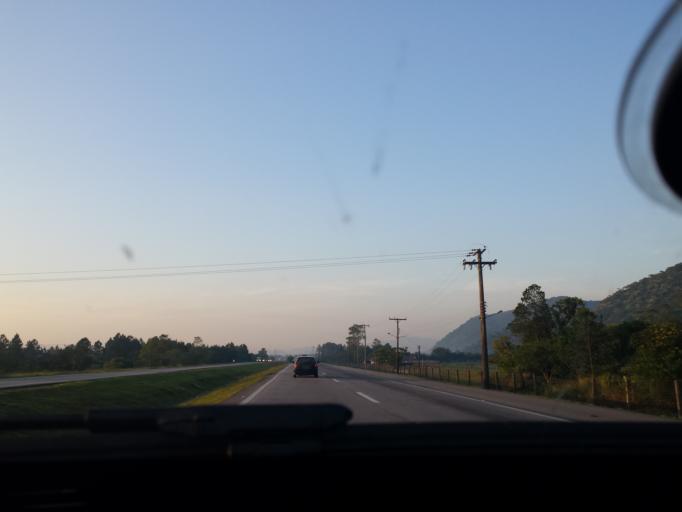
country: BR
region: Santa Catarina
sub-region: Florianopolis
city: Pantano do Sul
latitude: -27.8541
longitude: -48.6423
